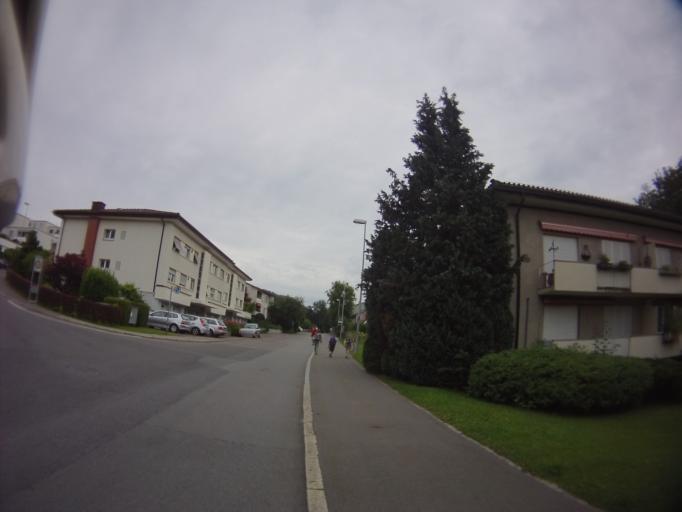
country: CH
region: Zurich
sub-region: Bezirk Horgen
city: Adliswil / Huendli-Zopf
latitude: 47.3164
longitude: 8.5179
